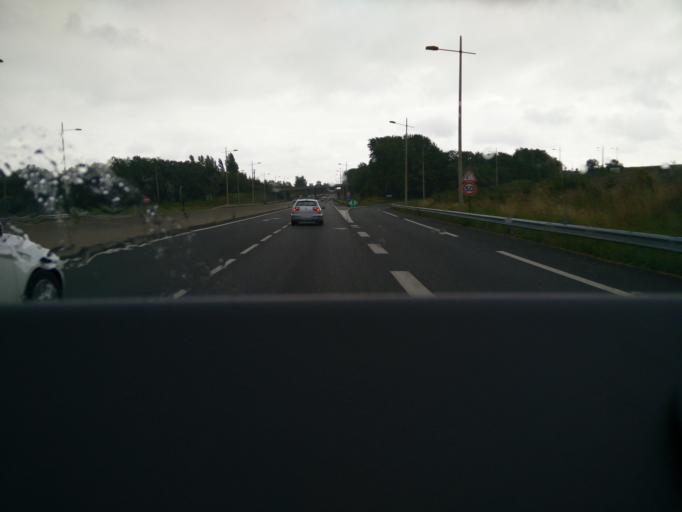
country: FR
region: Nord-Pas-de-Calais
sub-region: Departement du Pas-de-Calais
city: Aix-Noulette
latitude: 50.4353
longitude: 2.6968
